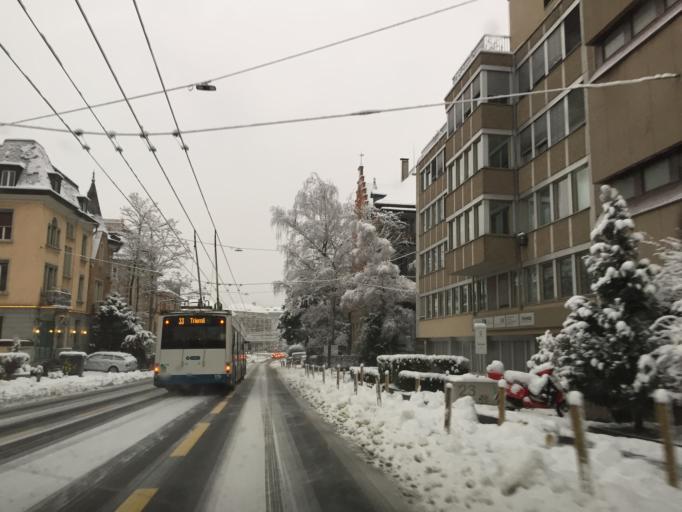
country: CH
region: Zurich
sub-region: Bezirk Zuerich
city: Zuerich (Kreis 6)
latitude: 47.3896
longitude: 8.5412
